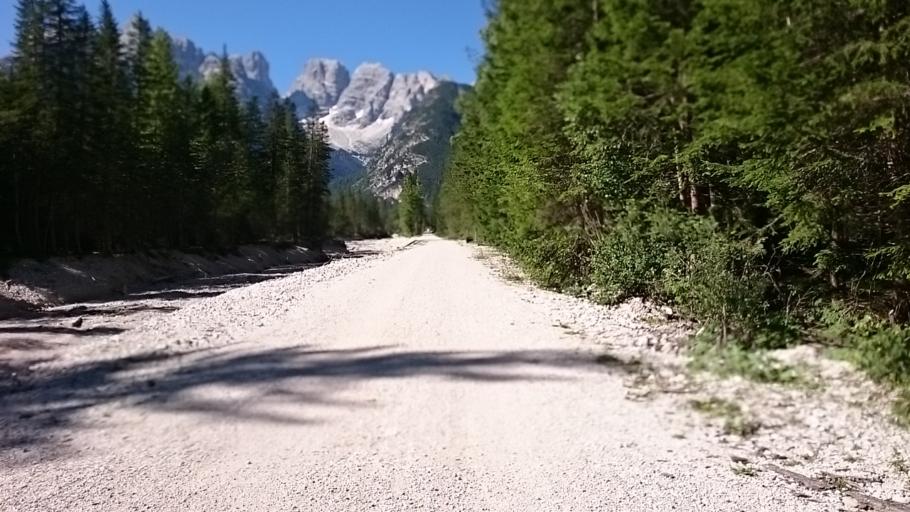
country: IT
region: Trentino-Alto Adige
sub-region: Bolzano
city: Dobbiaco
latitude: 46.6273
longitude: 12.2279
